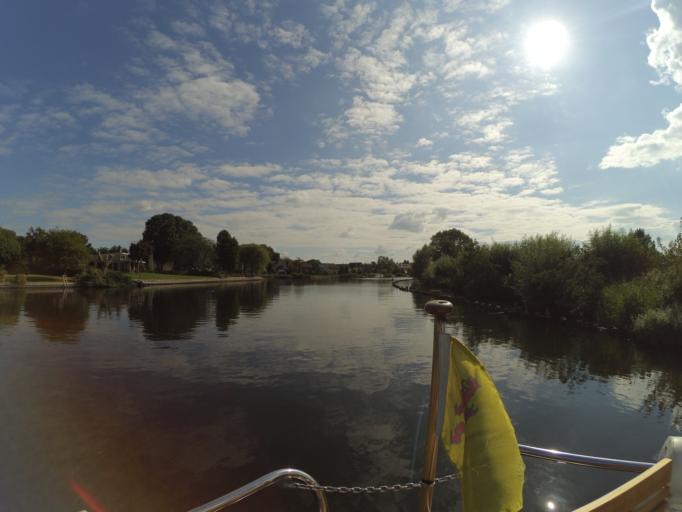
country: NL
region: Utrecht
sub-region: Stichtse Vecht
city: Vreeland
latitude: 52.2564
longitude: 5.0420
